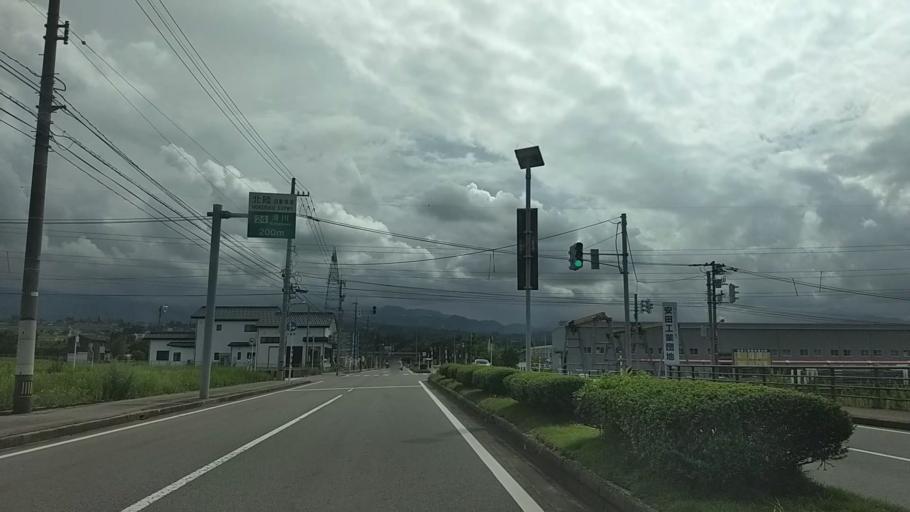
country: JP
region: Toyama
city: Kamiichi
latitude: 36.7462
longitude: 137.3766
